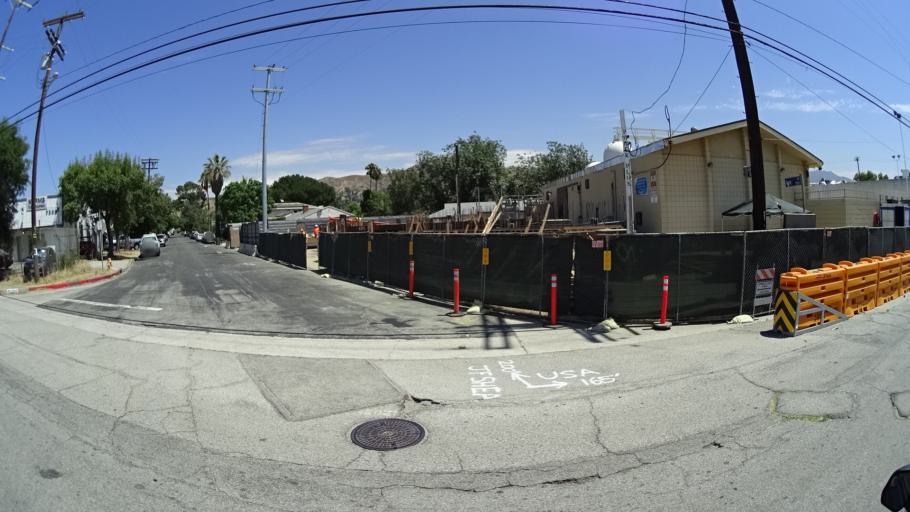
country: US
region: California
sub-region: Los Angeles County
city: North Hollywood
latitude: 34.2081
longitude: -118.3520
